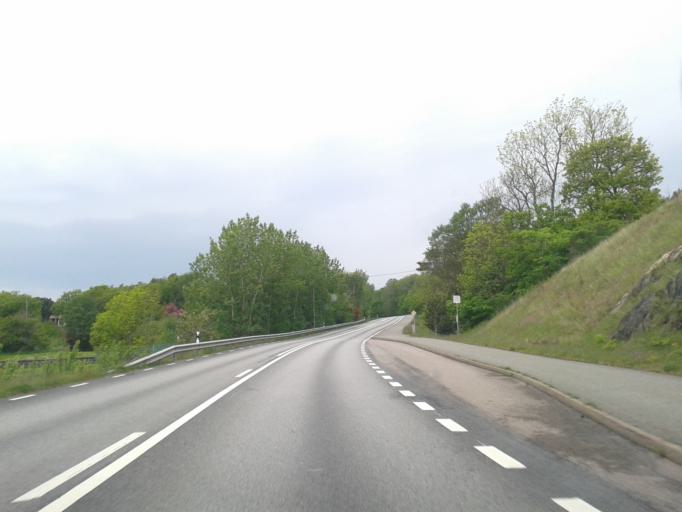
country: SE
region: Vaestra Goetaland
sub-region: Kungalvs Kommun
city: Marstrand
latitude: 57.8930
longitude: 11.6495
